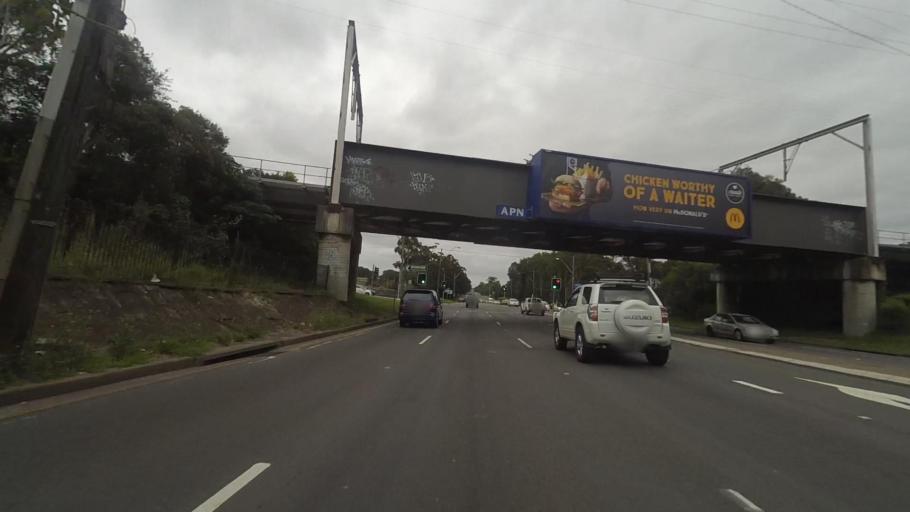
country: AU
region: New South Wales
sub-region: Auburn
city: Berala
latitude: -33.8852
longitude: 151.0399
